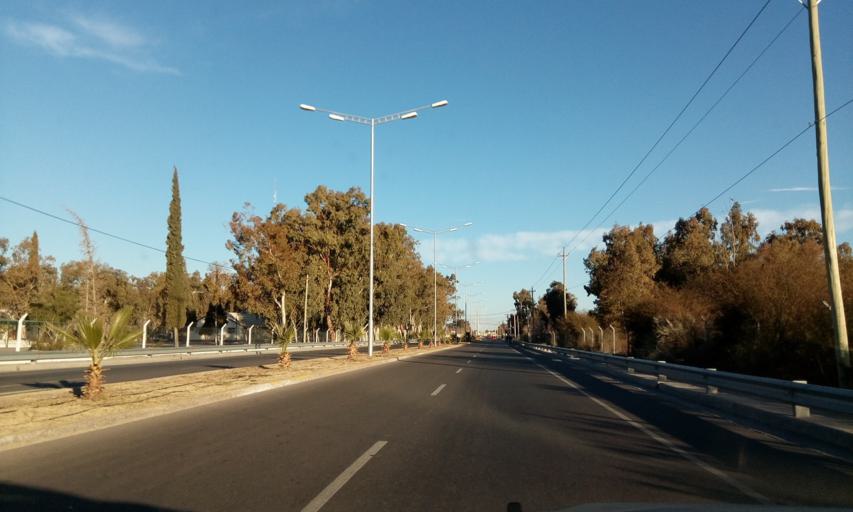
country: AR
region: San Juan
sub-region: Departamento de Rivadavia
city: Rivadavia
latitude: -31.5182
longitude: -68.6300
